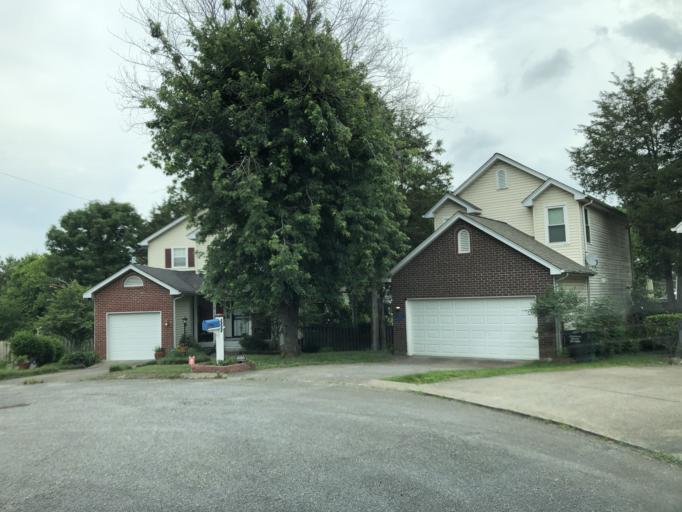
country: US
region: Tennessee
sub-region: Davidson County
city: Nashville
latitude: 36.2523
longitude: -86.7666
